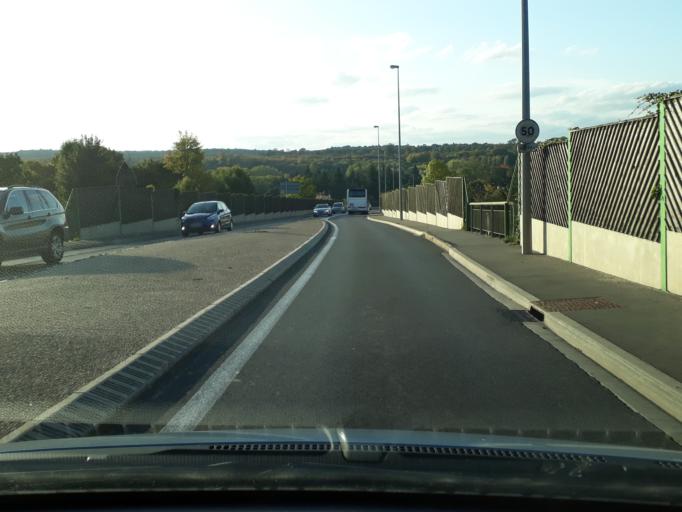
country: FR
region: Ile-de-France
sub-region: Departement de Seine-et-Marne
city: Samoreau
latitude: 48.4272
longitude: 2.7549
